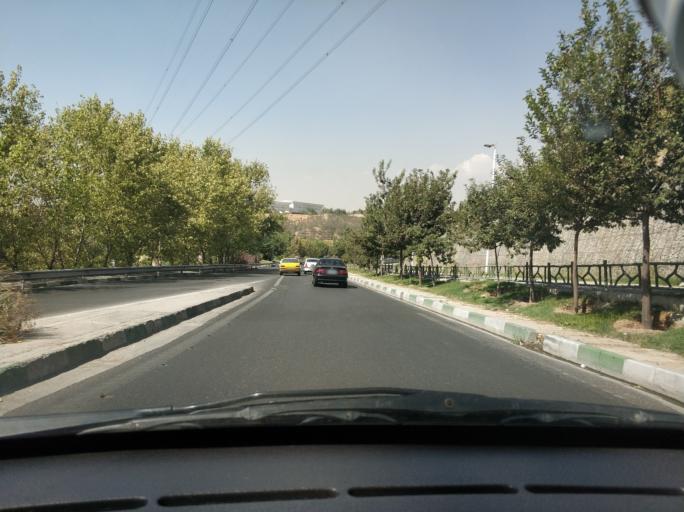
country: IR
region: Tehran
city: Tehran
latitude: 35.7416
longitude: 51.3715
